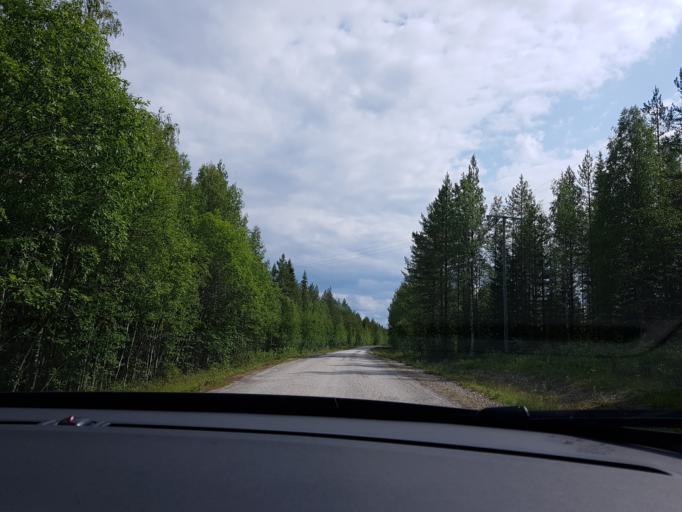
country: FI
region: Kainuu
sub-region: Kehys-Kainuu
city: Kuhmo
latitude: 64.4184
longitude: 29.7627
